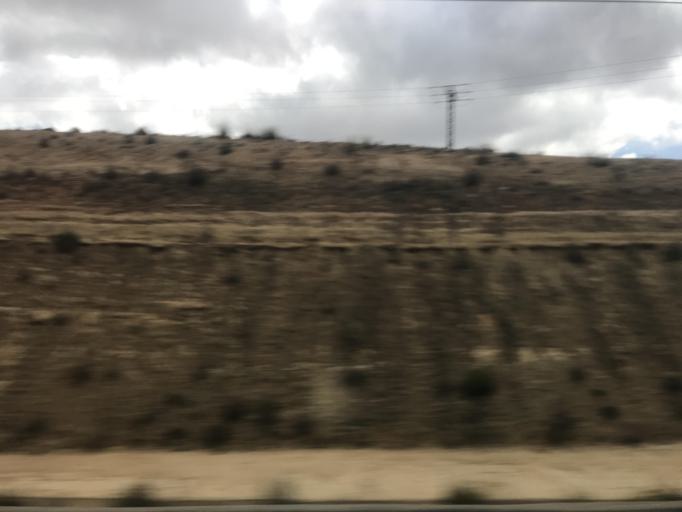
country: ES
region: Castille-La Mancha
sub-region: Provincia de Albacete
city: Almansa
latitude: 38.8764
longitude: -1.1636
